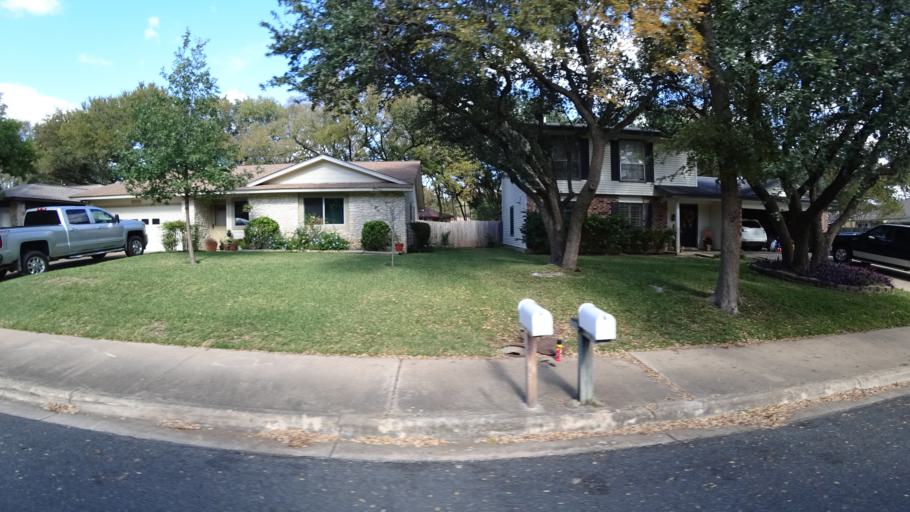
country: US
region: Texas
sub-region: Travis County
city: Wells Branch
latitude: 30.4173
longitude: -97.7252
